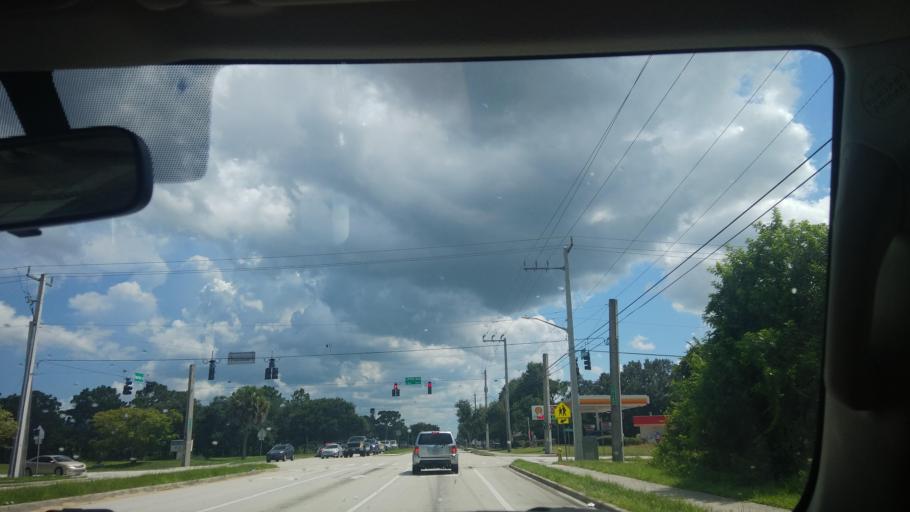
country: US
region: Florida
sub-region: Brevard County
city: Palm Bay
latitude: 27.9878
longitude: -80.6486
